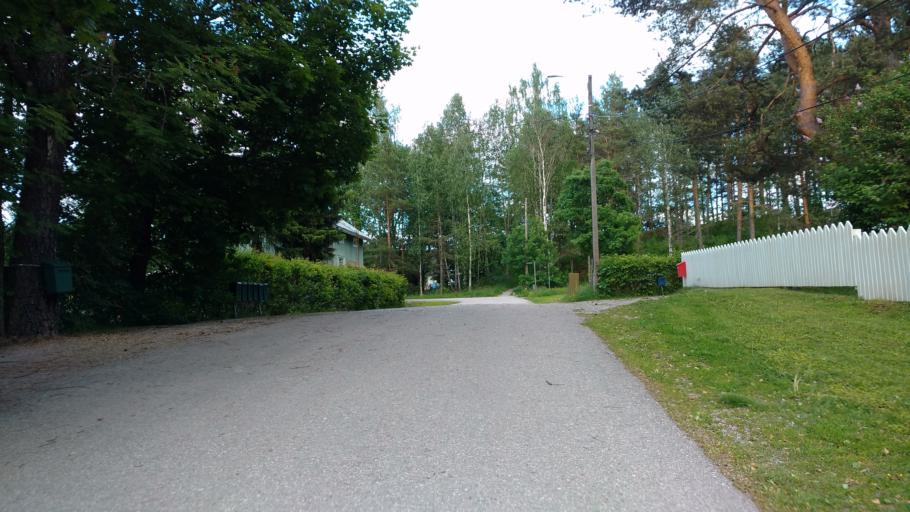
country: FI
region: Varsinais-Suomi
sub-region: Salo
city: Salo
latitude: 60.3862
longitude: 23.1548
